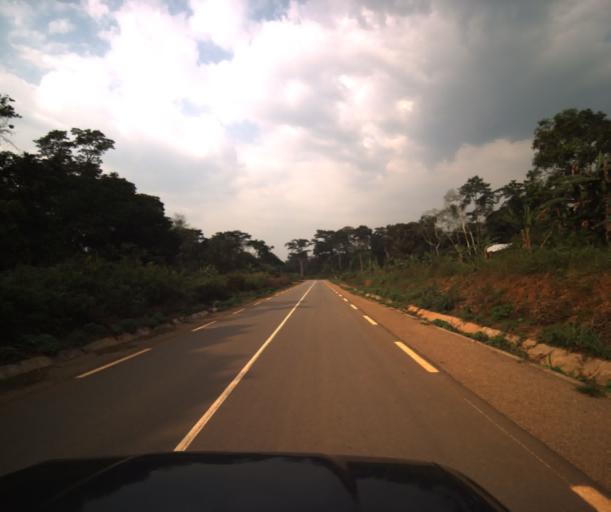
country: CM
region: Centre
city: Mbankomo
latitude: 3.7338
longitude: 11.3934
